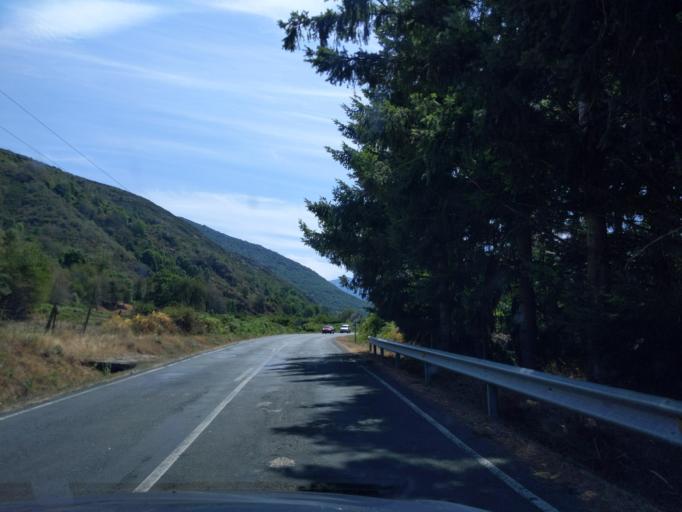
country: ES
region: La Rioja
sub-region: Provincia de La Rioja
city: Ezcaray
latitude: 42.2921
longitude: -3.0252
